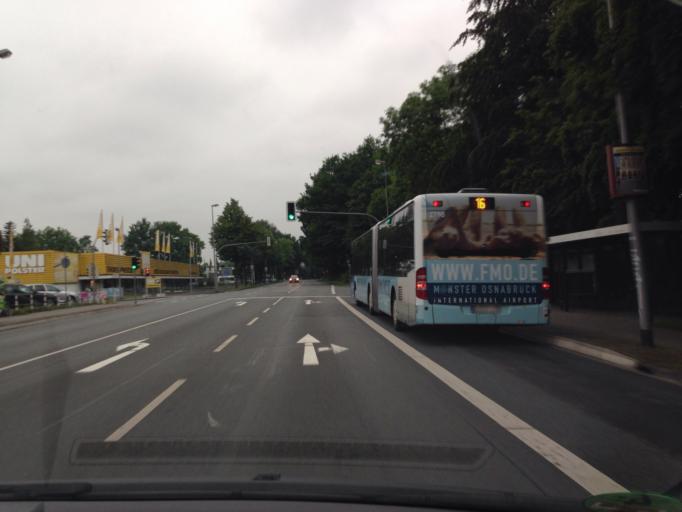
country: DE
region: North Rhine-Westphalia
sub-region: Regierungsbezirk Munster
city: Muenster
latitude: 51.9250
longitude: 7.5739
